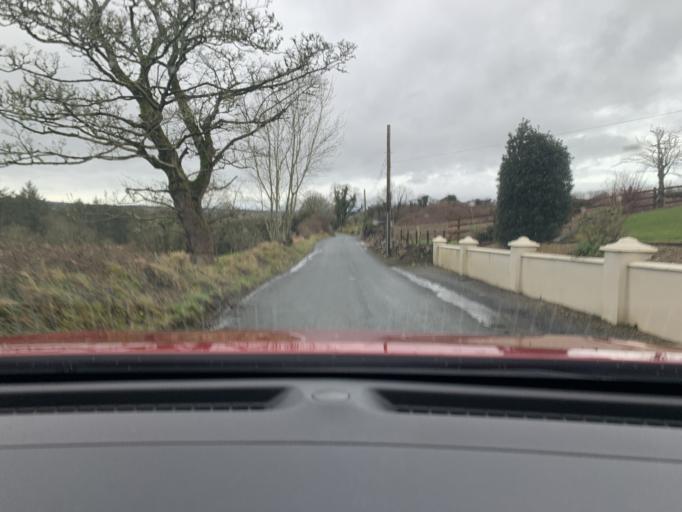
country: IE
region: Connaught
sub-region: Sligo
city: Collooney
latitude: 54.2014
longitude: -8.4371
